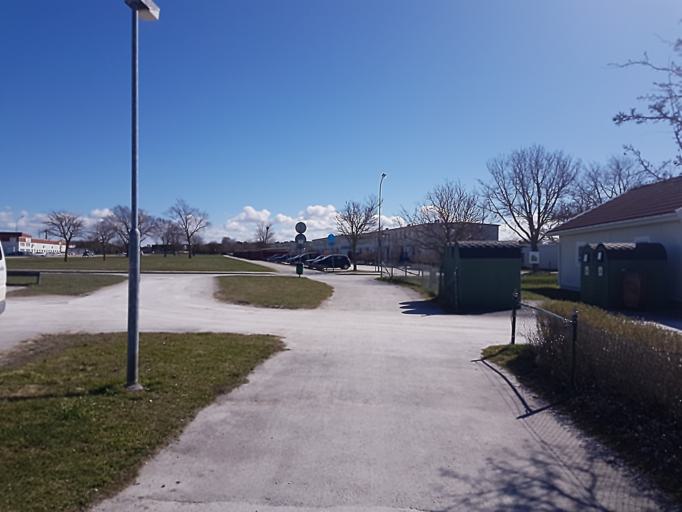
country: SE
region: Gotland
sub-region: Gotland
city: Visby
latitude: 57.6413
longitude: 18.3193
